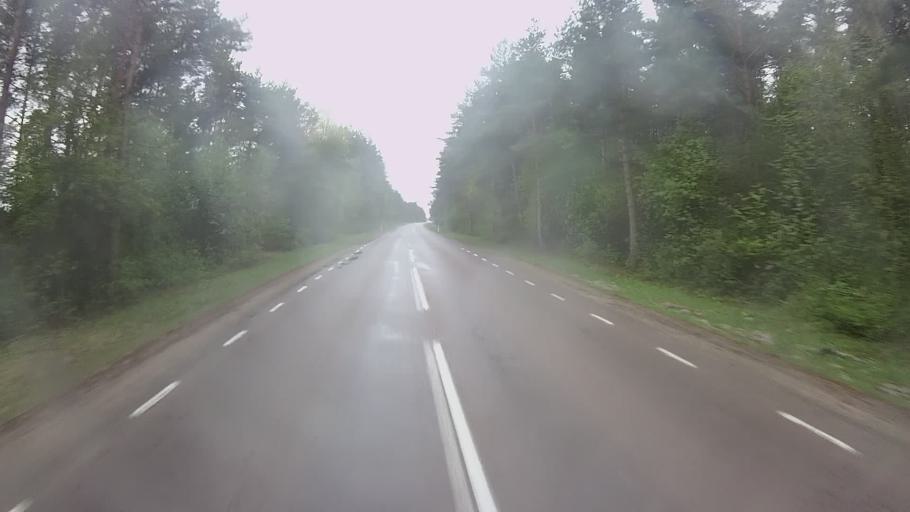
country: EE
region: Saare
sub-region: Kuressaare linn
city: Kuressaare
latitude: 58.3452
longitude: 22.5841
